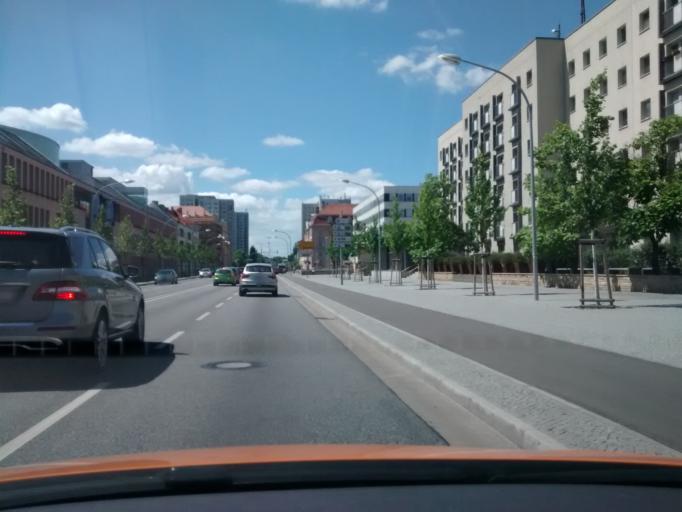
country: DE
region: Brandenburg
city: Potsdam
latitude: 52.3951
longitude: 13.0553
